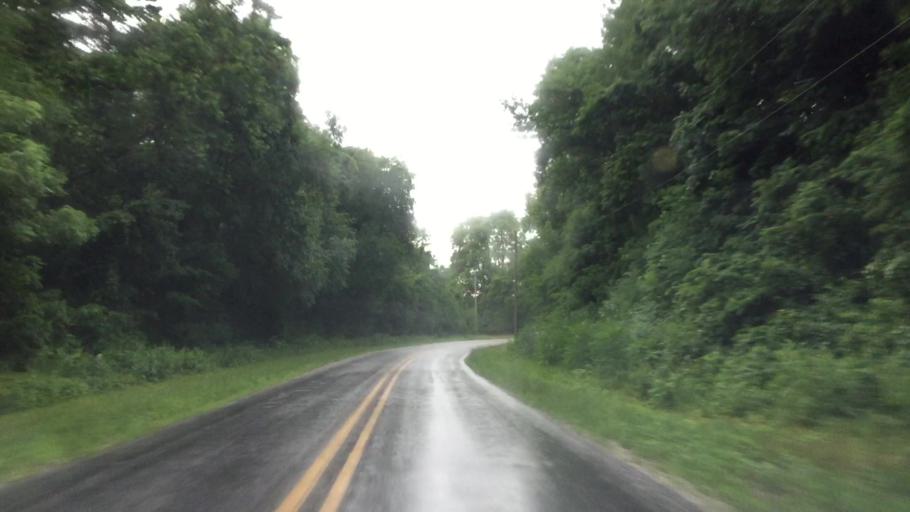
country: US
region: Iowa
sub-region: Lee County
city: Fort Madison
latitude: 40.6106
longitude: -91.2813
